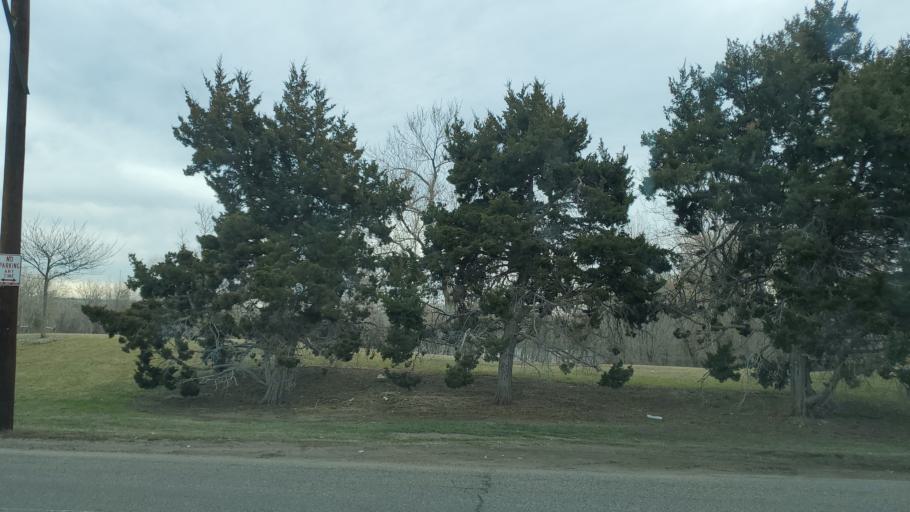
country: US
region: Colorado
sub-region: Denver County
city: Denver
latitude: 39.6989
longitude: -104.9968
